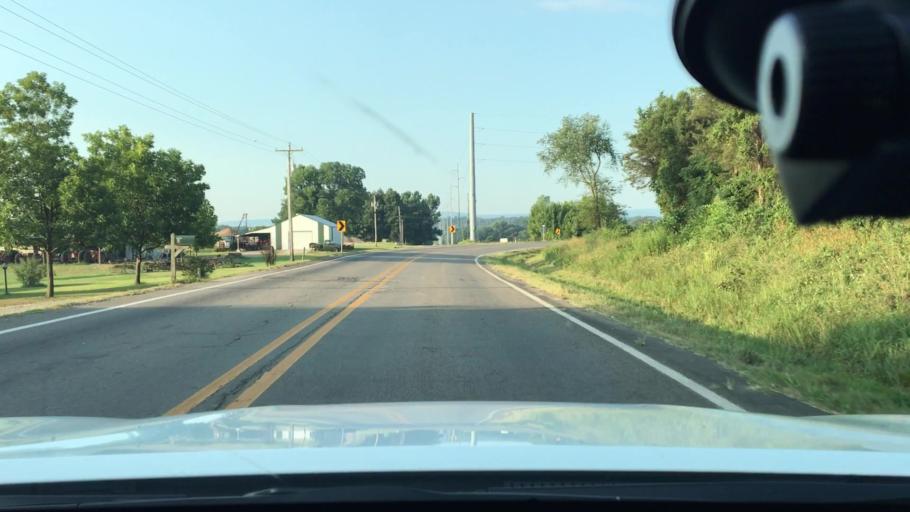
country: US
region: Arkansas
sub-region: Johnson County
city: Coal Hill
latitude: 35.3764
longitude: -93.5613
